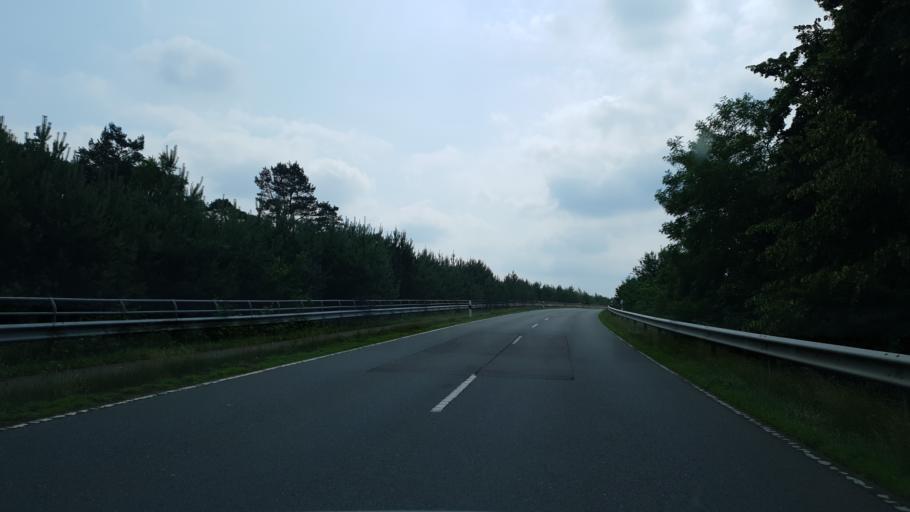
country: DE
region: Lower Saxony
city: Wietmarschen
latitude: 52.5549
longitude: 7.1944
